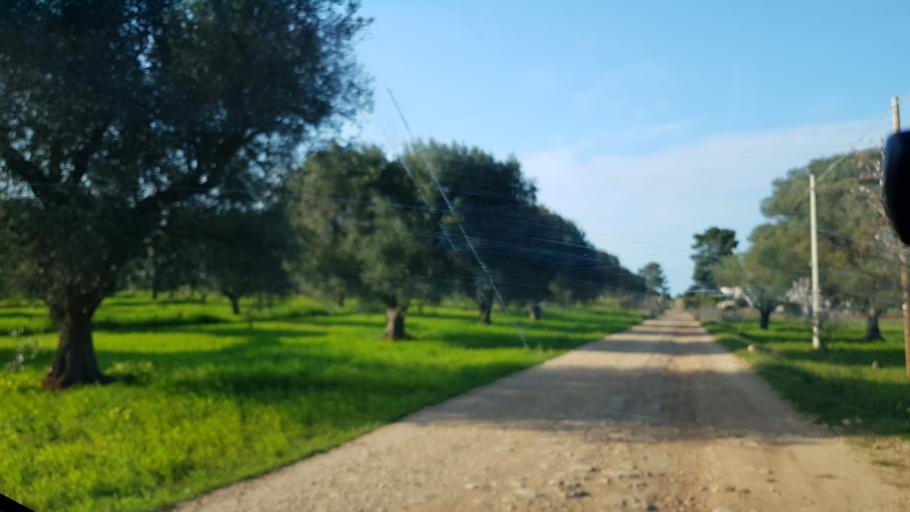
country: IT
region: Apulia
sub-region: Provincia di Brindisi
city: San Vito dei Normanni
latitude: 40.6782
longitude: 17.7894
